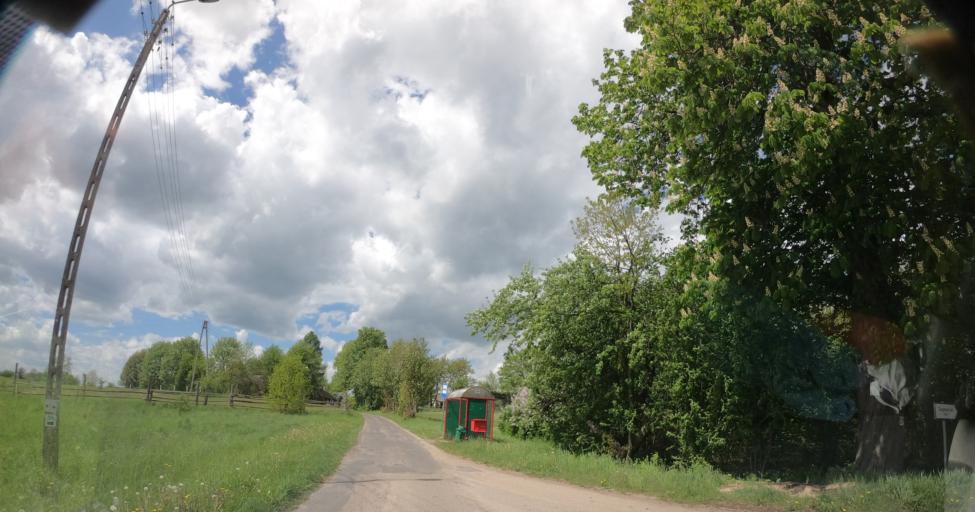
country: PL
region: West Pomeranian Voivodeship
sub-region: Powiat drawski
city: Drawsko Pomorskie
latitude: 53.5735
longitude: 15.7680
